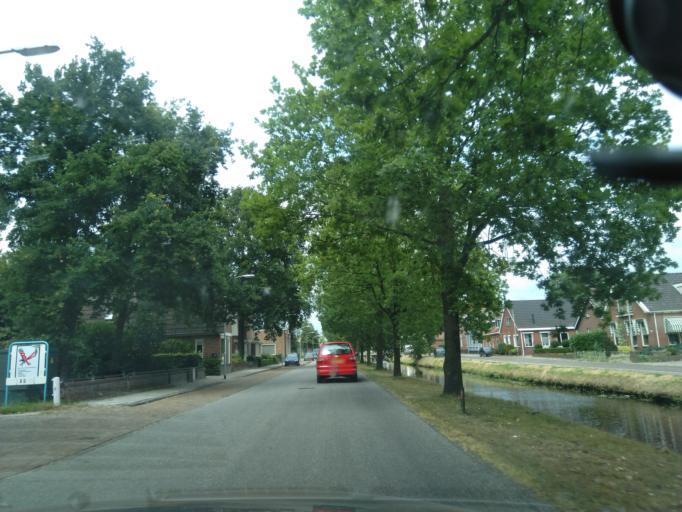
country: NL
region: Groningen
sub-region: Gemeente Pekela
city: Oude Pekela
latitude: 53.0862
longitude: 6.9791
